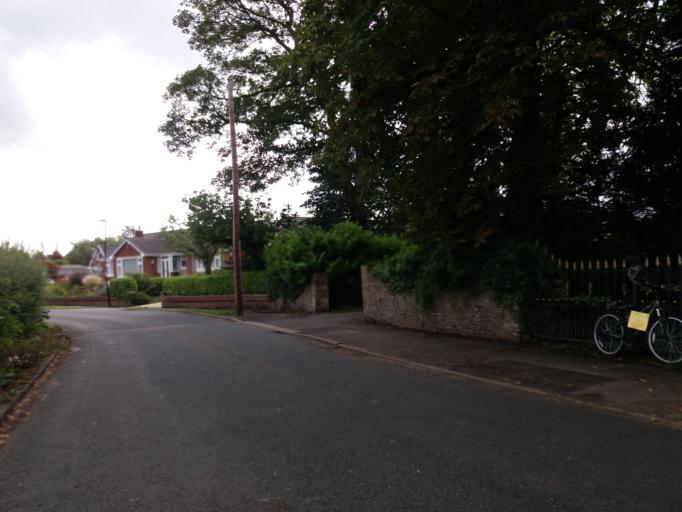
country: GB
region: England
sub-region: Lancashire
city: Euxton
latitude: 53.6630
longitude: -2.6611
